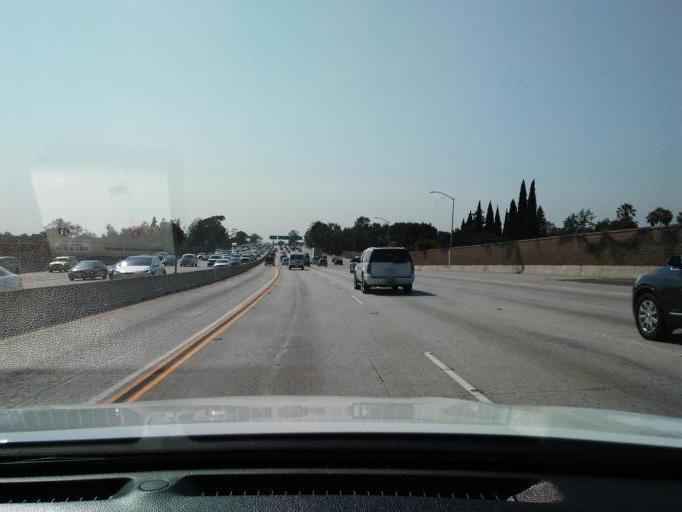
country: US
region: California
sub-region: Los Angeles County
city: Signal Hill
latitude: 33.8203
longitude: -118.1929
